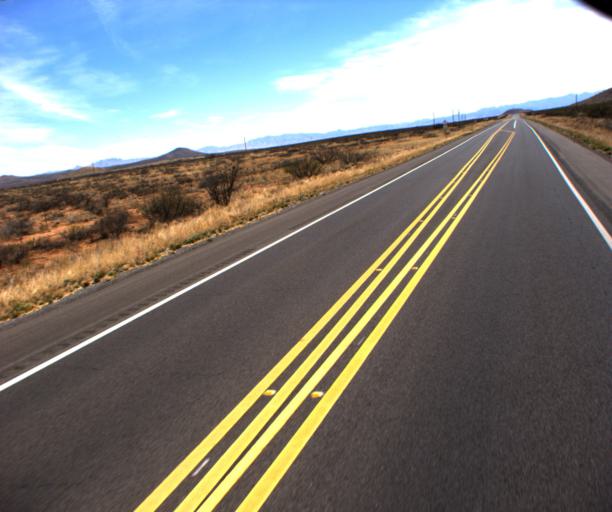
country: US
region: Arizona
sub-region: Cochise County
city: Willcox
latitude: 31.9055
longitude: -109.7664
